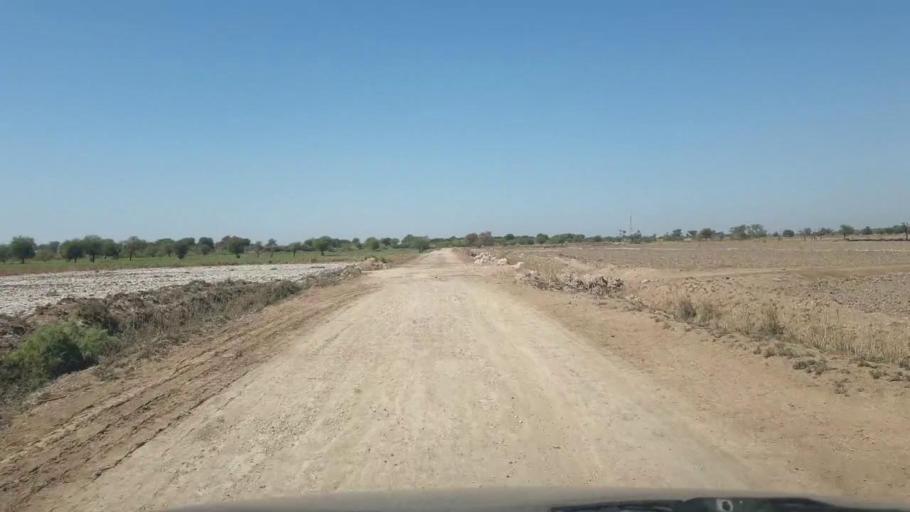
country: PK
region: Sindh
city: Dhoro Naro
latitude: 25.4505
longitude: 69.6116
